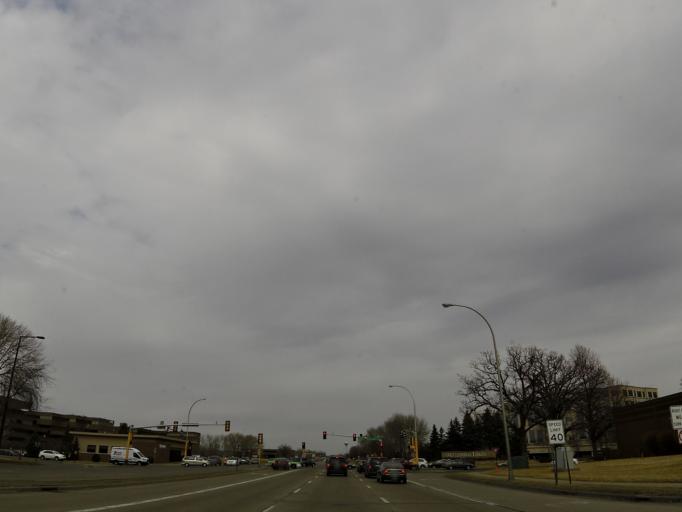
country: US
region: Minnesota
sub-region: Hennepin County
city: Edina
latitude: 44.8613
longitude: -93.3287
